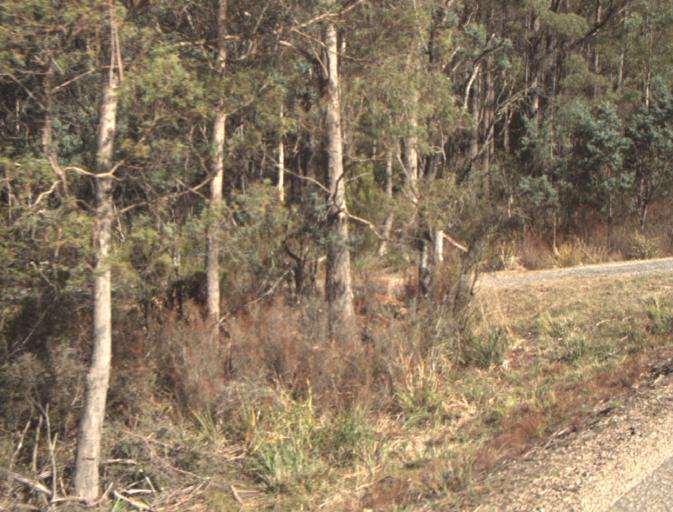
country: AU
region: Tasmania
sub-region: Launceston
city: Mayfield
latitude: -41.3185
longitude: 147.1909
